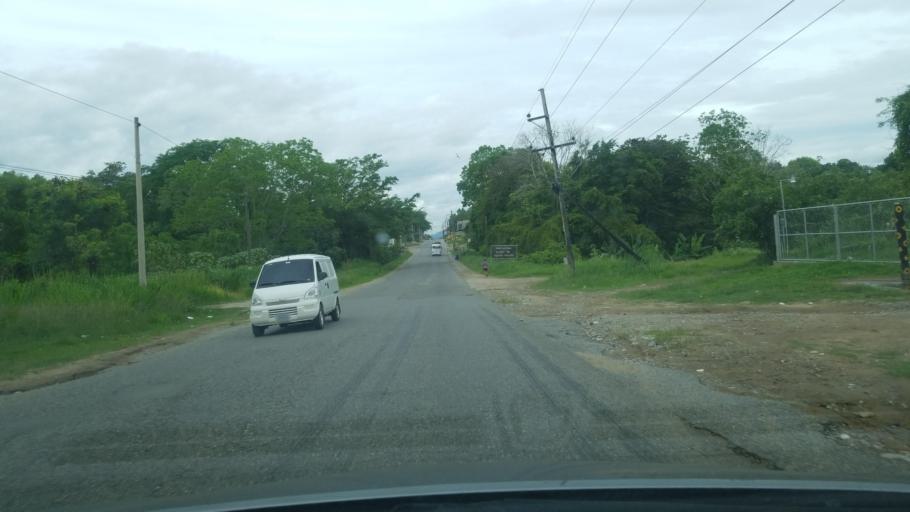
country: HN
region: Santa Barbara
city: La Flecha
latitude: 15.2977
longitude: -88.4840
